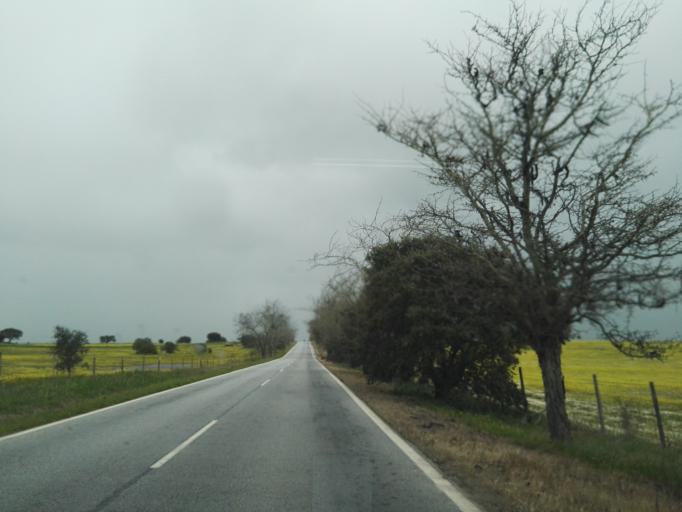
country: PT
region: Portalegre
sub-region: Arronches
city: Arronches
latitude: 39.0337
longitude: -7.2582
